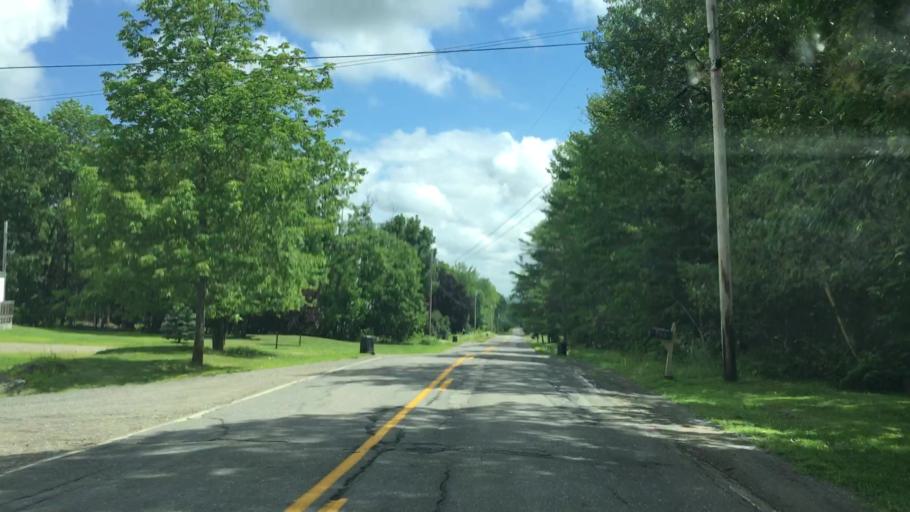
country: US
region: Maine
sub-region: Penobscot County
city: Carmel
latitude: 44.7945
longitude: -69.0701
